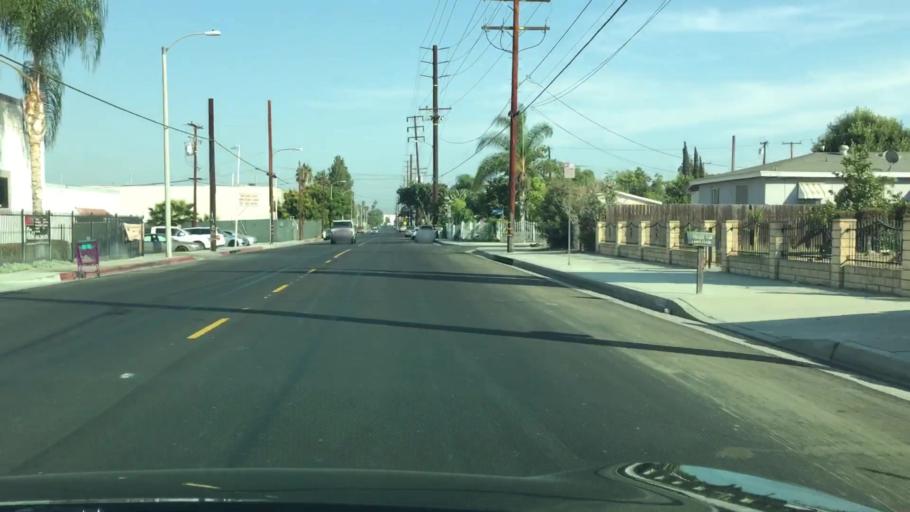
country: US
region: California
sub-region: Los Angeles County
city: Avocado Heights
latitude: 34.0218
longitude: -117.9822
